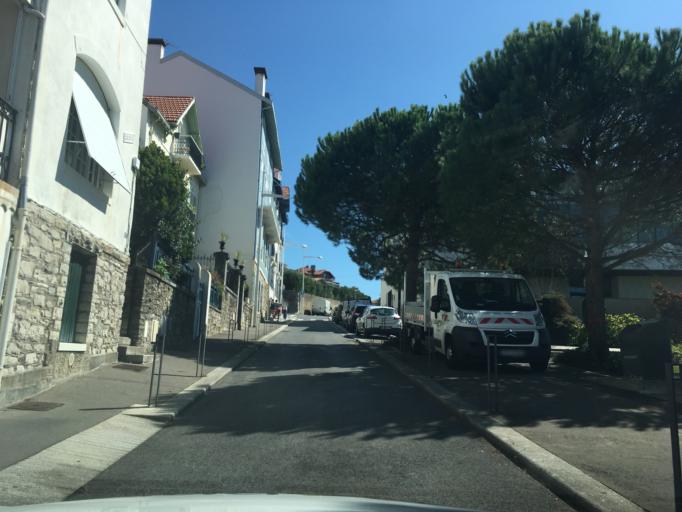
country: FR
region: Aquitaine
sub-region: Departement des Pyrenees-Atlantiques
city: Biarritz
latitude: 43.4813
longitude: -1.5539
